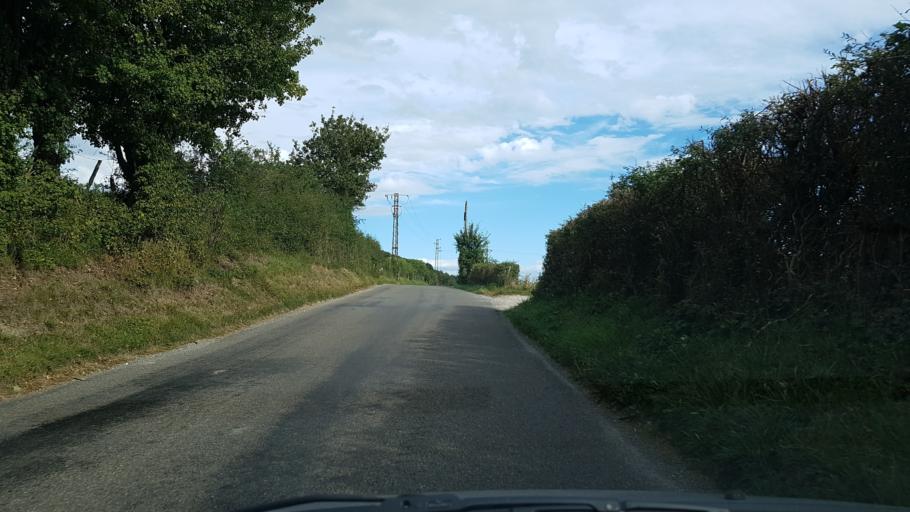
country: FR
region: Rhone-Alpes
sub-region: Departement de l'Ain
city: Ceyzeriat
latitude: 46.1614
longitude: 5.3416
